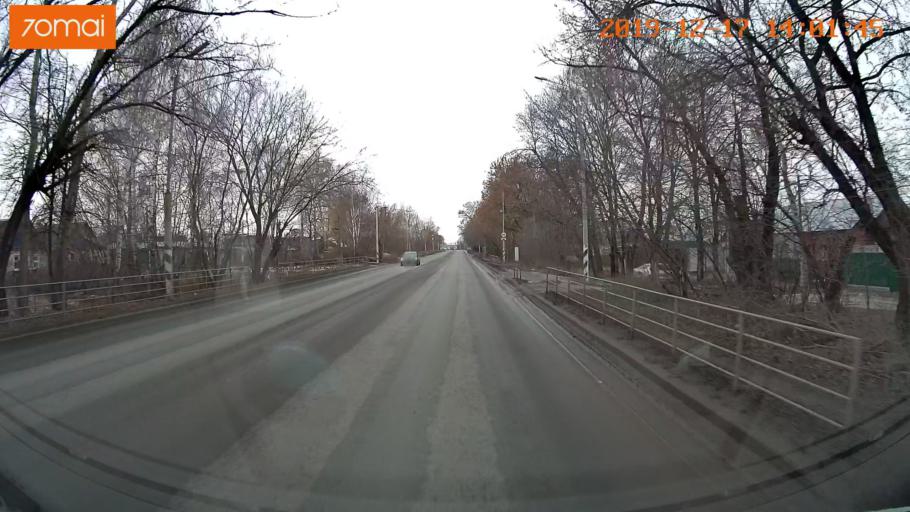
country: RU
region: Rjazan
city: Ryazan'
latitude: 54.6181
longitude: 39.6543
